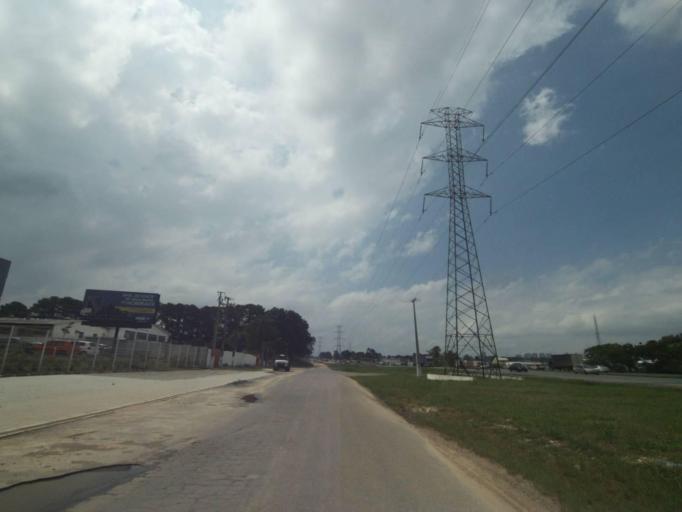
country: BR
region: Parana
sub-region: Curitiba
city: Curitiba
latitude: -25.4772
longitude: -49.3512
